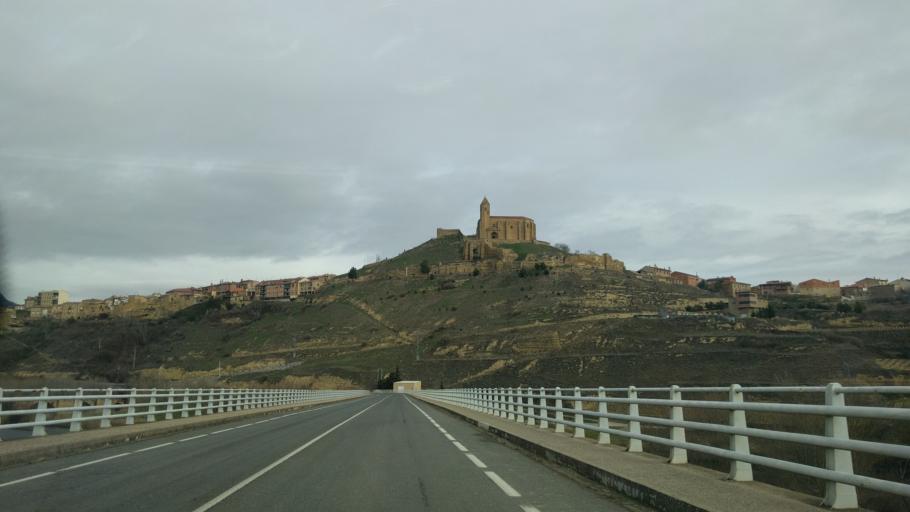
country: ES
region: La Rioja
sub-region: Provincia de La Rioja
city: San Vicente de la Sonsierra
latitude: 42.5567
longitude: -2.7618
